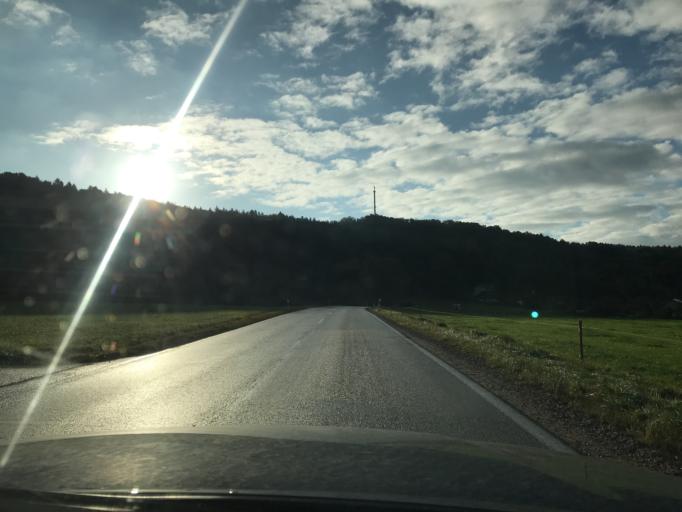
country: DE
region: Bavaria
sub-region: Upper Bavaria
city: Geretsried
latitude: 47.8668
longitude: 11.5145
